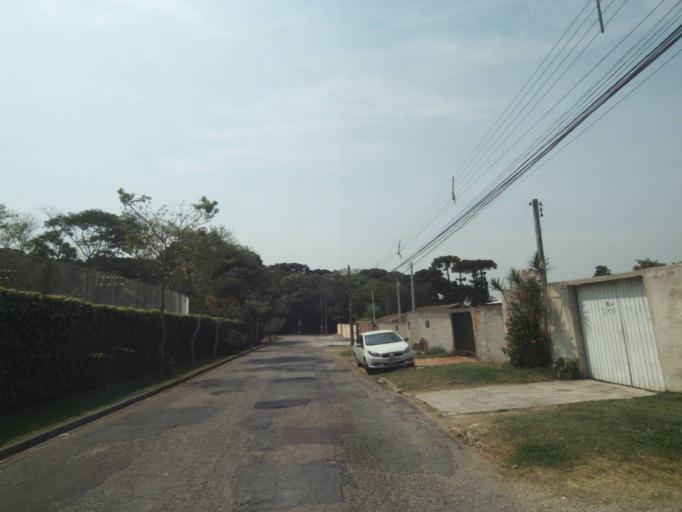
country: BR
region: Parana
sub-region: Sao Jose Dos Pinhais
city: Sao Jose dos Pinhais
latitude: -25.4909
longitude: -49.2092
